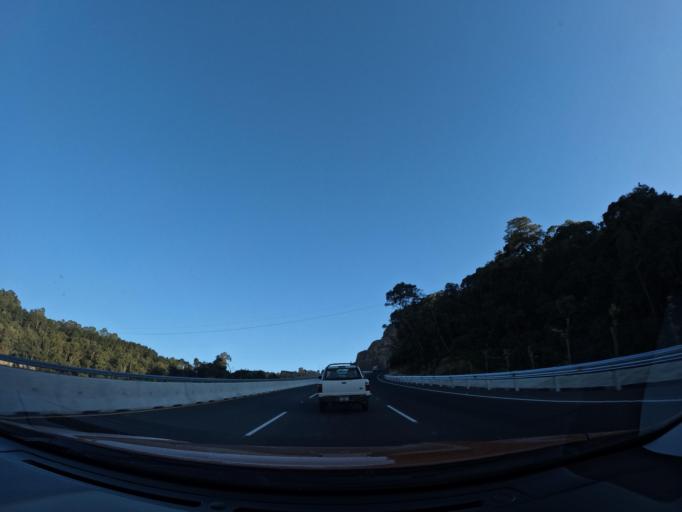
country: GT
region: Guatemala
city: Villa Canales
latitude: 14.4852
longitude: -90.4903
